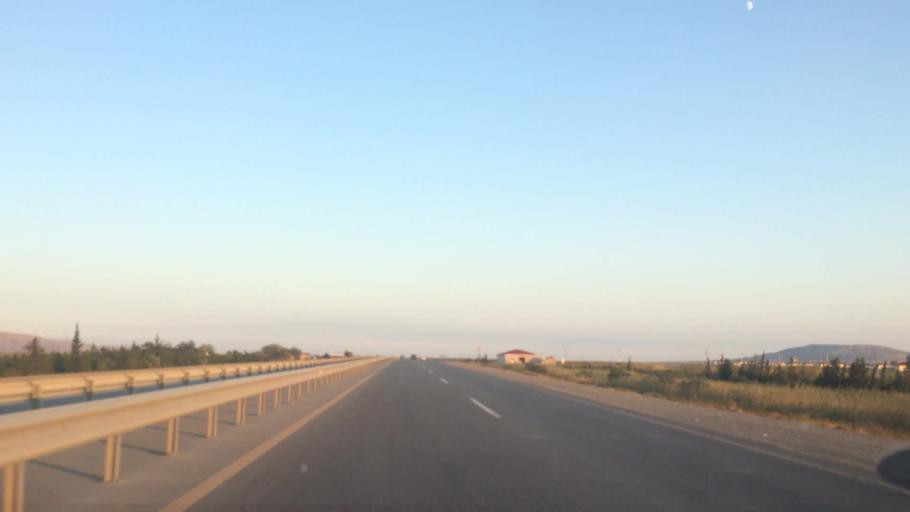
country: AZ
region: Baki
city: Qobustan
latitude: 39.9865
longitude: 49.2073
